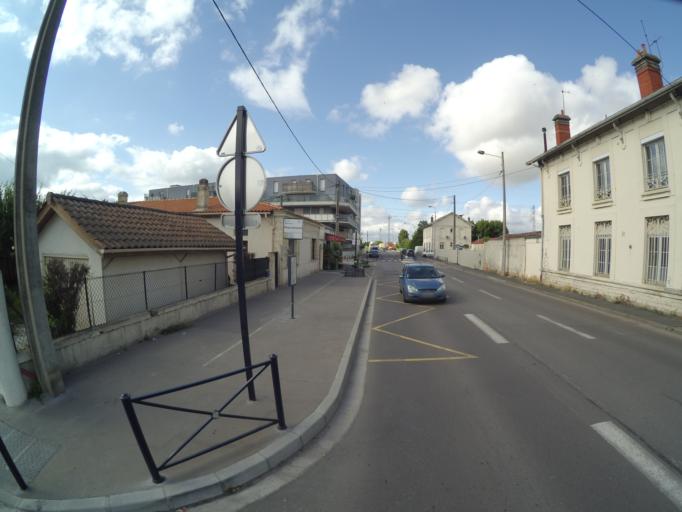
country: FR
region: Aquitaine
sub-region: Departement de la Gironde
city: Lormont
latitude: 44.8839
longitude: -0.5502
